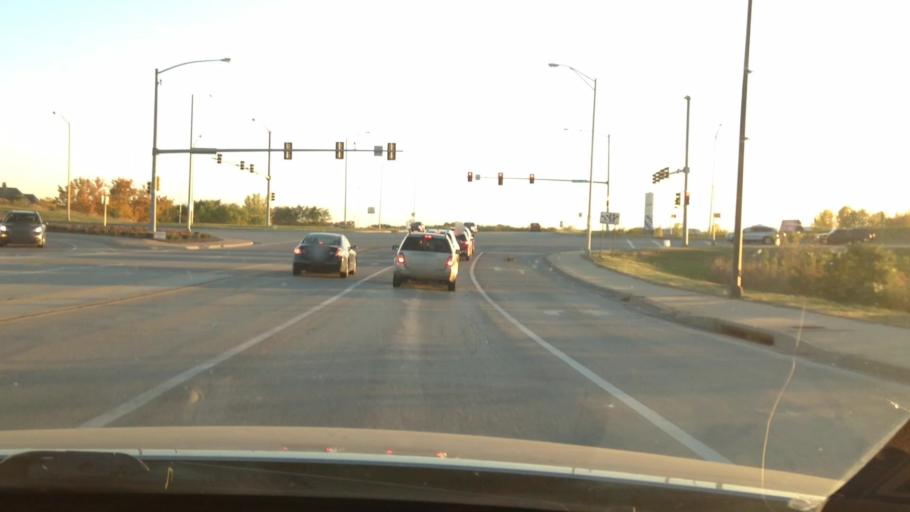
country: US
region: Kansas
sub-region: Wyandotte County
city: Edwardsville
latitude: 39.1175
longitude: -94.8191
